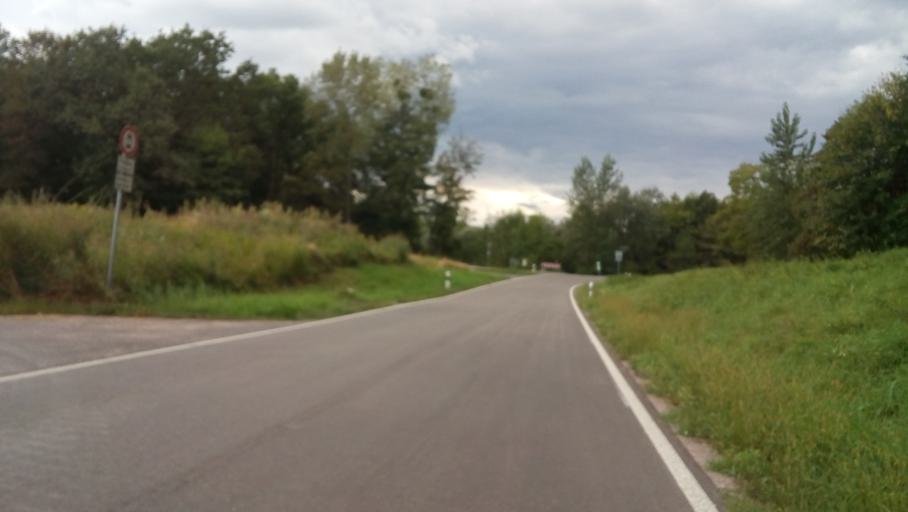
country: DE
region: Baden-Wuerttemberg
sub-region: Karlsruhe Region
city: Greffern
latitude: 48.7493
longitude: 7.9881
